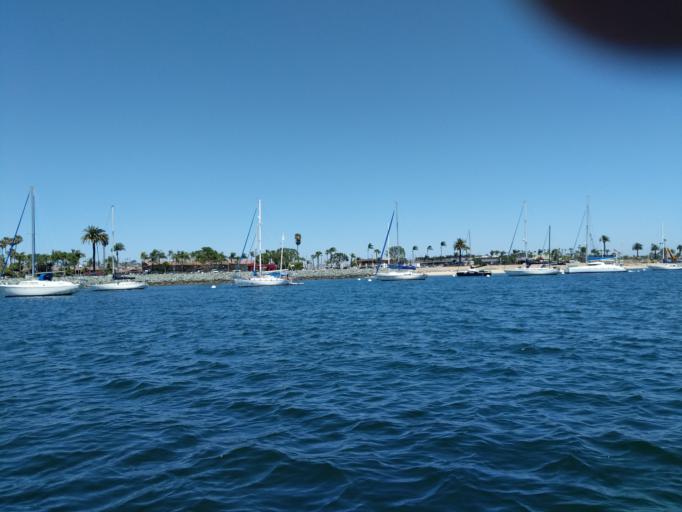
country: US
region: California
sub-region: San Diego County
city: Coronado
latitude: 32.7118
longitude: -117.2254
